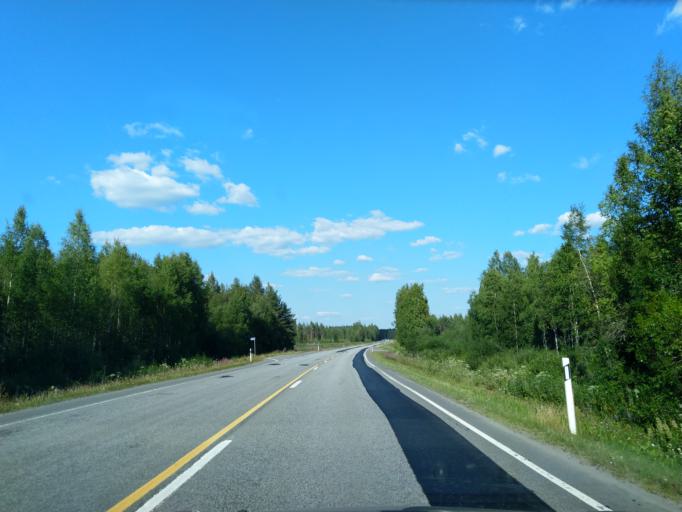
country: FI
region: Pirkanmaa
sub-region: Luoteis-Pirkanmaa
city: Kihnioe
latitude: 62.1276
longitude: 23.1182
